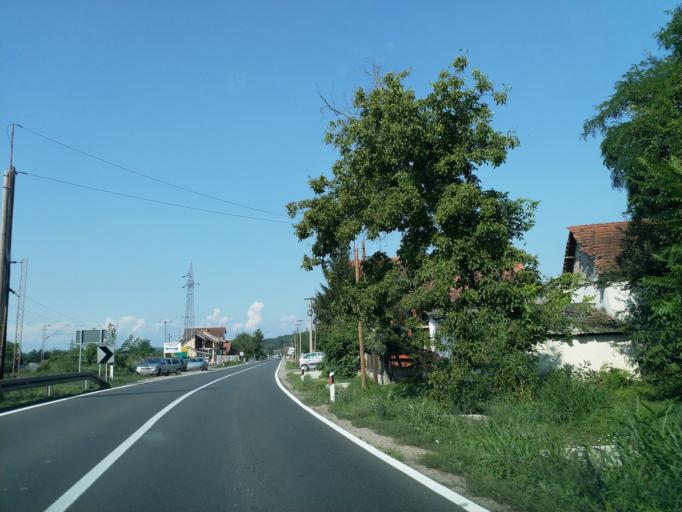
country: RS
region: Central Serbia
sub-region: Rasinski Okrug
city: Cicevac
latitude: 43.6969
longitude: 21.4246
